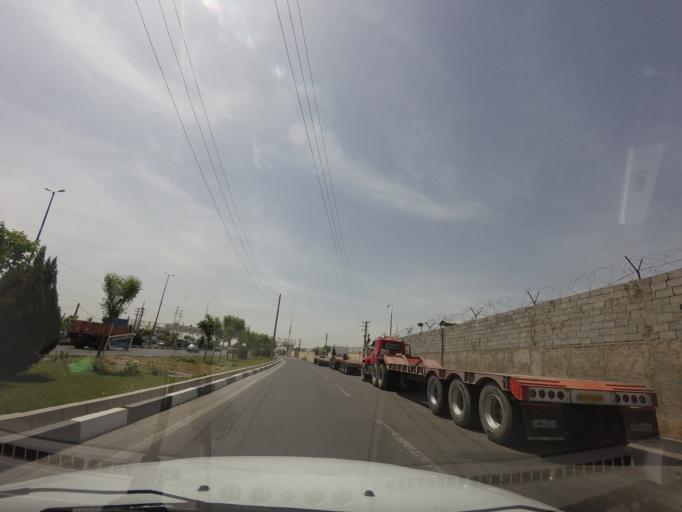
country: IR
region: Tehran
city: Eslamshahr
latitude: 35.5789
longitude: 51.2672
